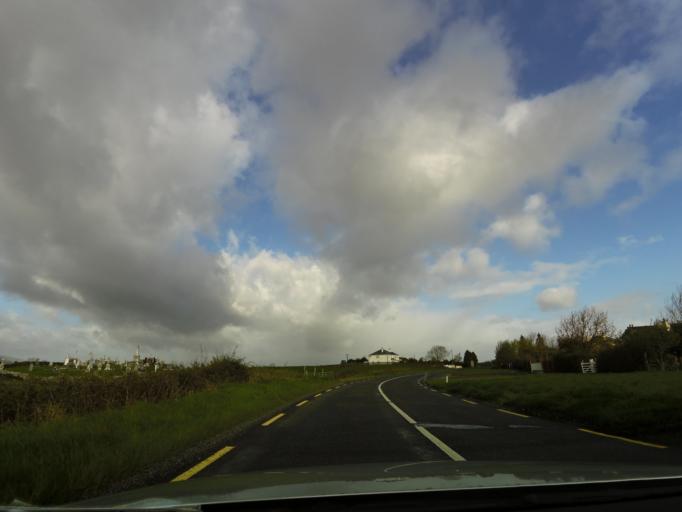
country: IE
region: Munster
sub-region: North Tipperary
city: Nenagh
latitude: 52.8328
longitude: -8.1219
